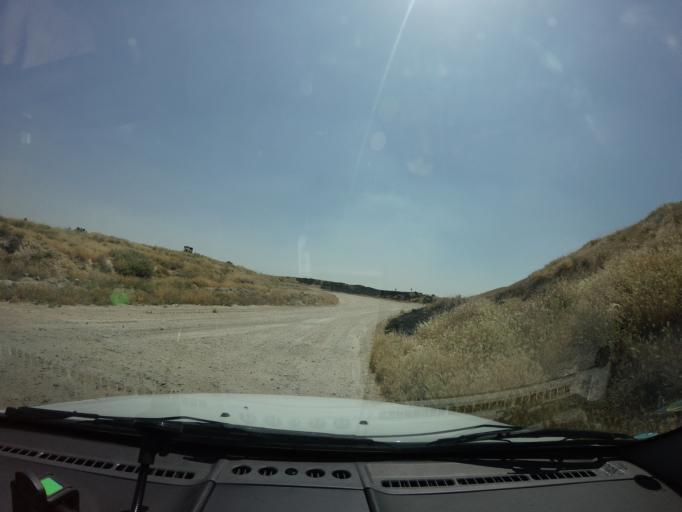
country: IR
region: Tehran
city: Eslamshahr
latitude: 35.4718
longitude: 51.2375
